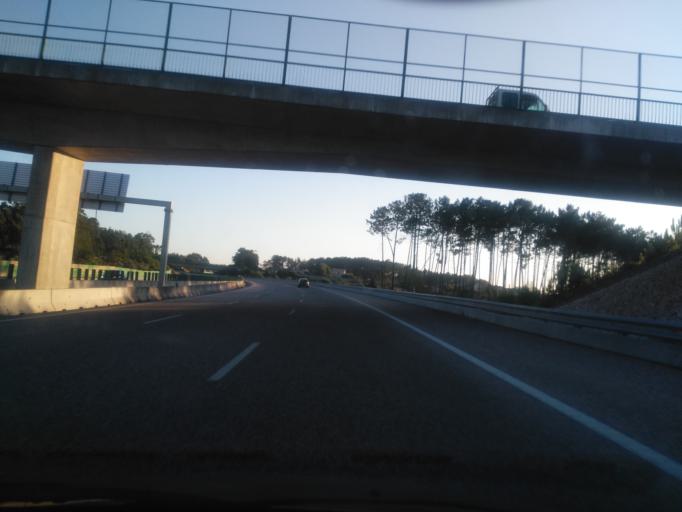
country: PT
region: Leiria
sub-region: Leiria
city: Monte Redondo
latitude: 39.9324
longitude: -8.7776
